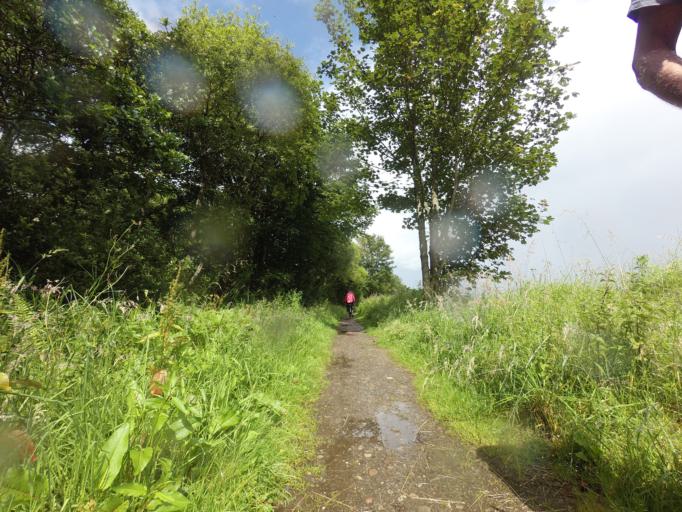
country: GB
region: Scotland
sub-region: Moray
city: Fochabers
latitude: 57.6663
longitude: -3.0914
